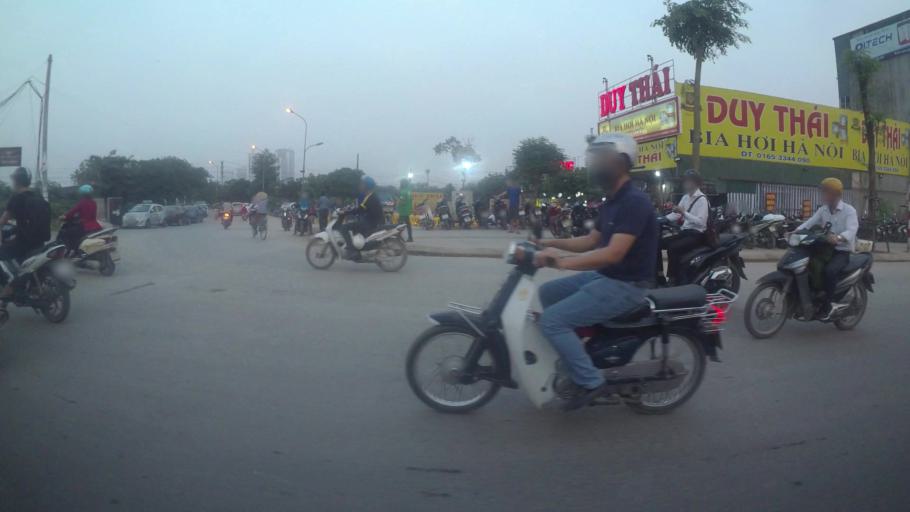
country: VN
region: Ha Noi
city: Tay Ho
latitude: 21.0612
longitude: 105.7839
